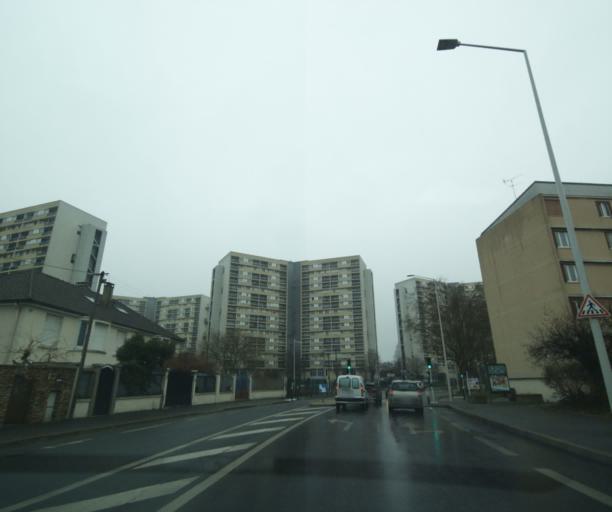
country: FR
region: Ile-de-France
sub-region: Departement des Hauts-de-Seine
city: Nanterre
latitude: 48.8979
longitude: 2.2065
